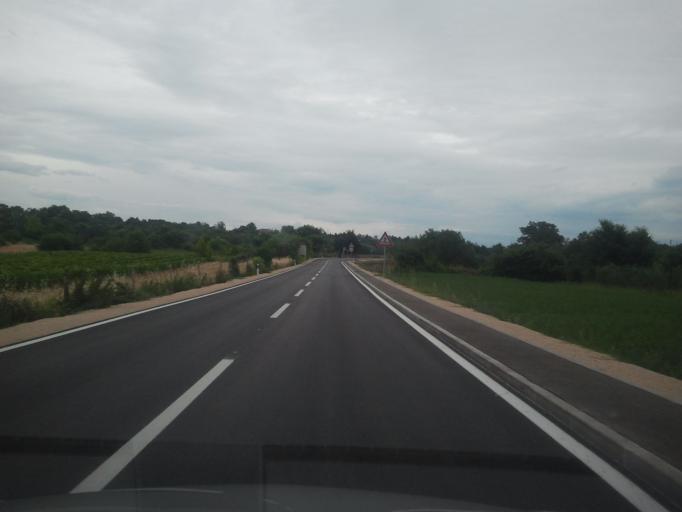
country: HR
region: Zadarska
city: Benkovac
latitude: 44.0214
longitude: 15.5920
